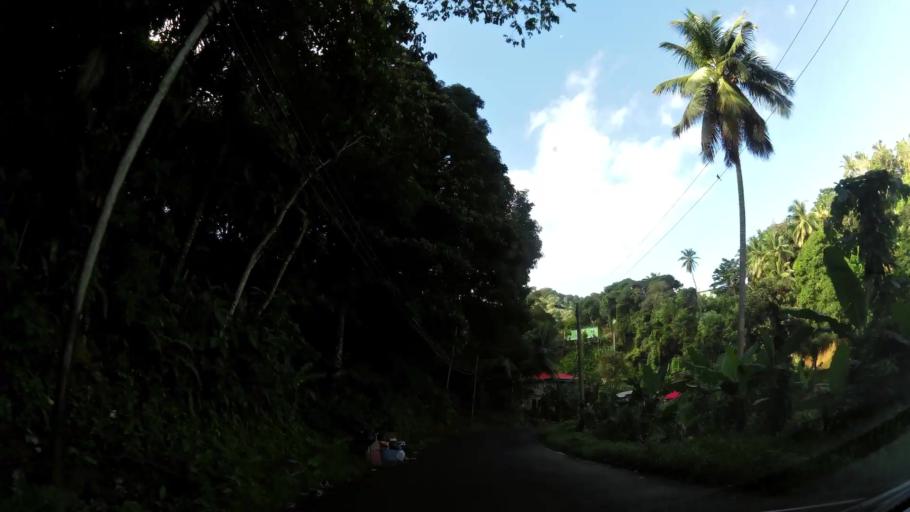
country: DM
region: Saint Andrew
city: Calibishie
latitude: 15.5912
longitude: -61.3817
